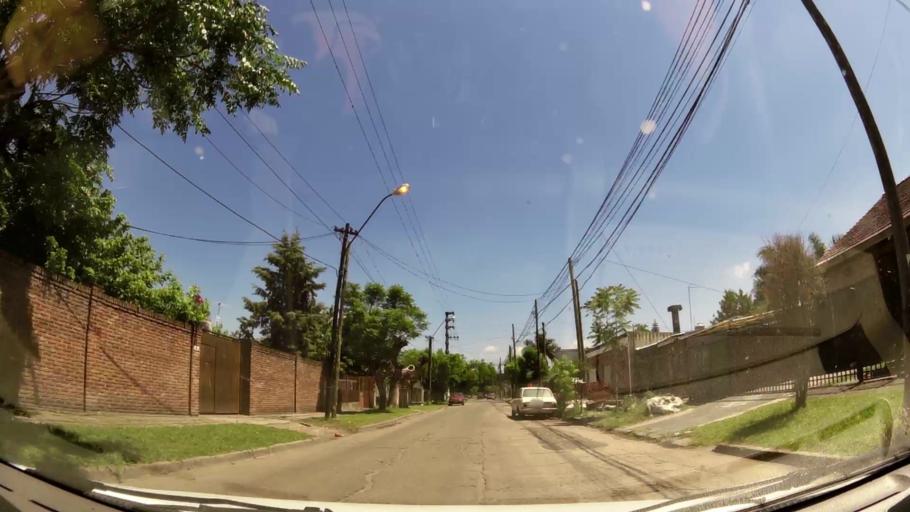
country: AR
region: Buenos Aires
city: Ituzaingo
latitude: -34.6549
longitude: -58.6819
